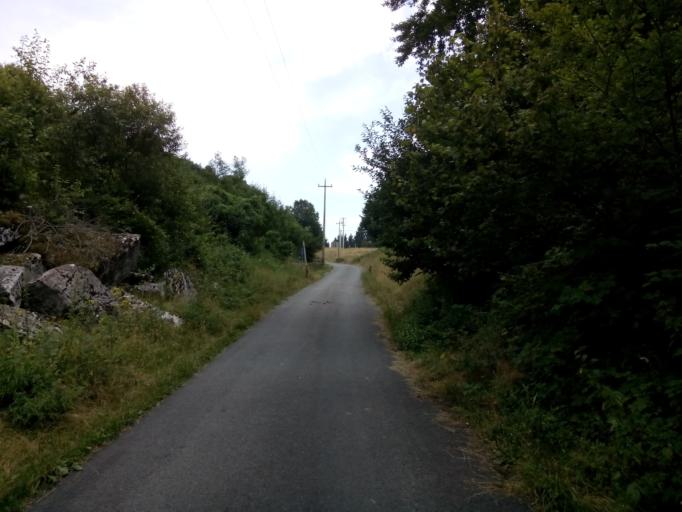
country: IT
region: Veneto
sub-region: Provincia di Vicenza
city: Campolongo sul Brenta
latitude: 45.8058
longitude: 11.6720
